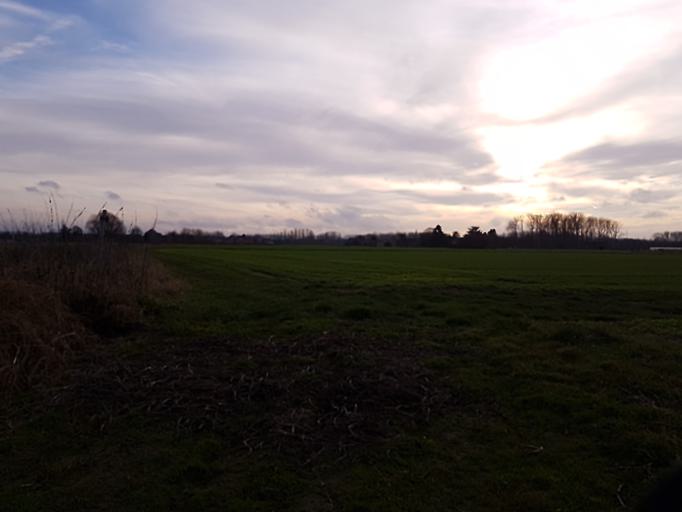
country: BE
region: Flanders
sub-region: Provincie Vlaams-Brabant
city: Rotselaar
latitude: 50.9535
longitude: 4.7025
